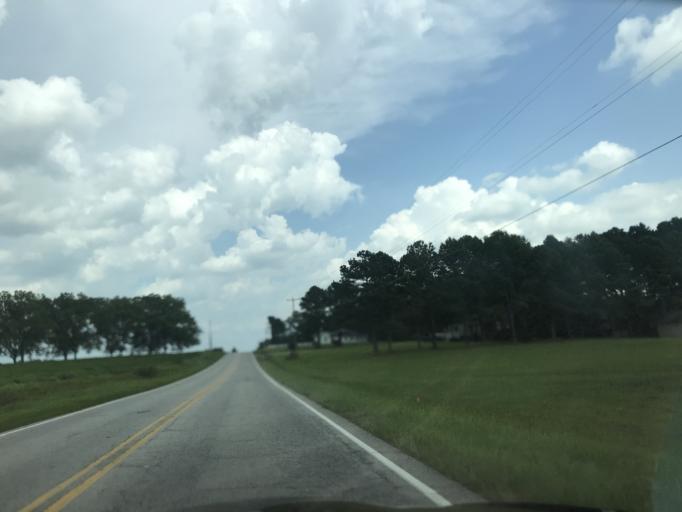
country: US
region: North Carolina
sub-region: Johnston County
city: Four Oaks
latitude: 35.5121
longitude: -78.5293
